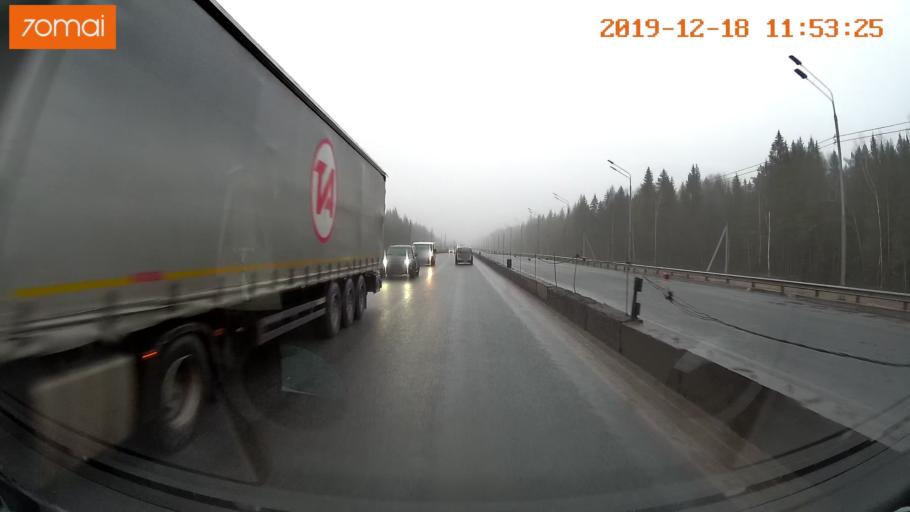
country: RU
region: Moskovskaya
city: Yershovo
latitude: 55.8040
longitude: 36.9200
